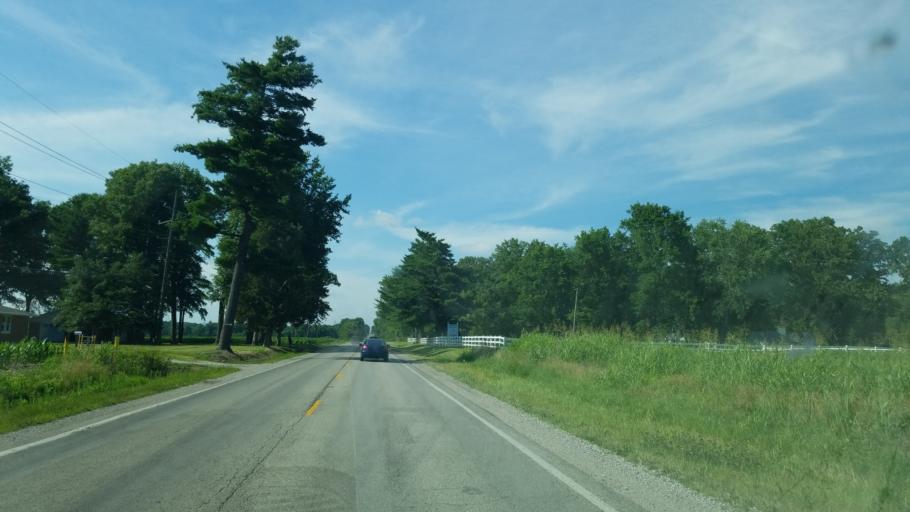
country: US
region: Illinois
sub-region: Saint Clair County
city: Lebanon
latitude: 38.5850
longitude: -89.8078
